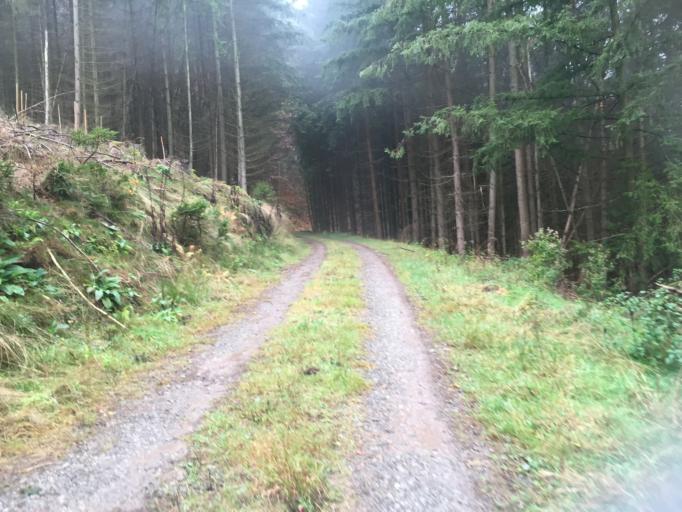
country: DE
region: Baden-Wuerttemberg
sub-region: Karlsruhe Region
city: Heddesbach
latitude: 49.4625
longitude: 8.8583
